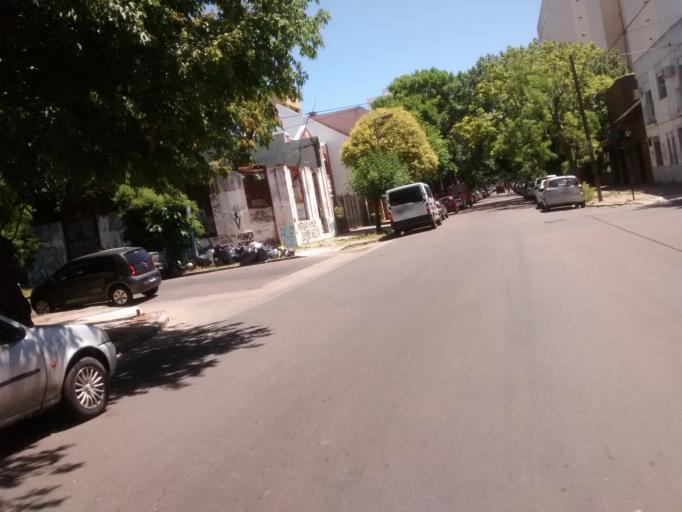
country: AR
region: Buenos Aires
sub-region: Partido de La Plata
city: La Plata
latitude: -34.9234
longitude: -57.9359
